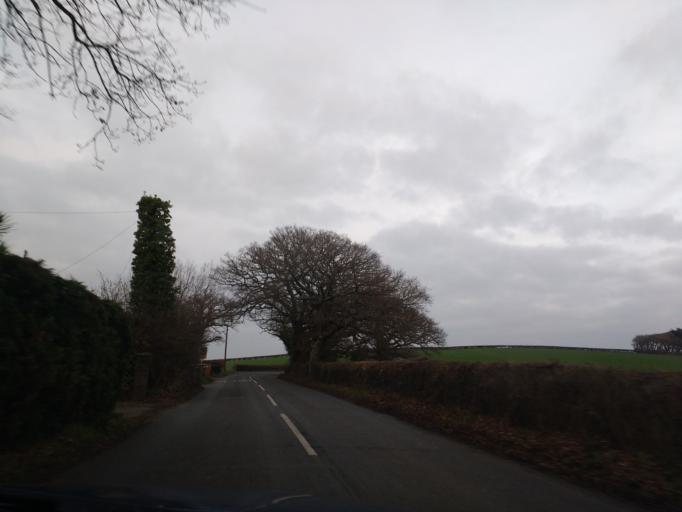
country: GB
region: England
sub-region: Isle of Wight
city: Northwood
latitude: 50.7262
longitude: -1.3537
